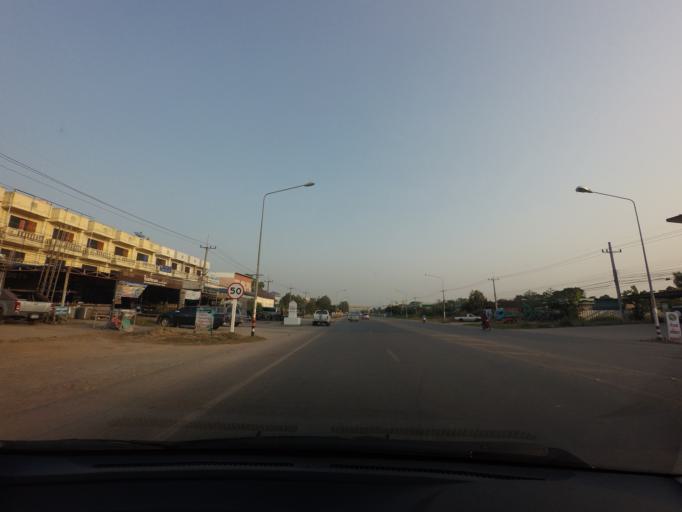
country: TH
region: Sukhothai
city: Sukhothai
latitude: 17.0175
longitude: 99.8306
